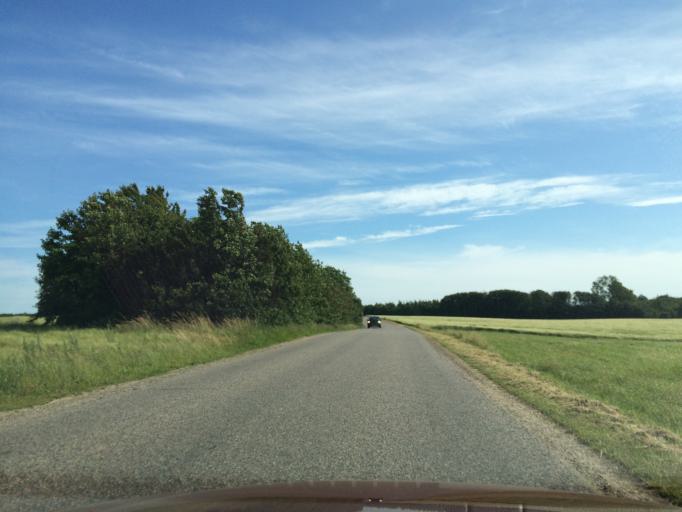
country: DK
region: Central Jutland
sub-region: Silkeborg Kommune
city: Silkeborg
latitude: 56.2160
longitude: 9.5613
